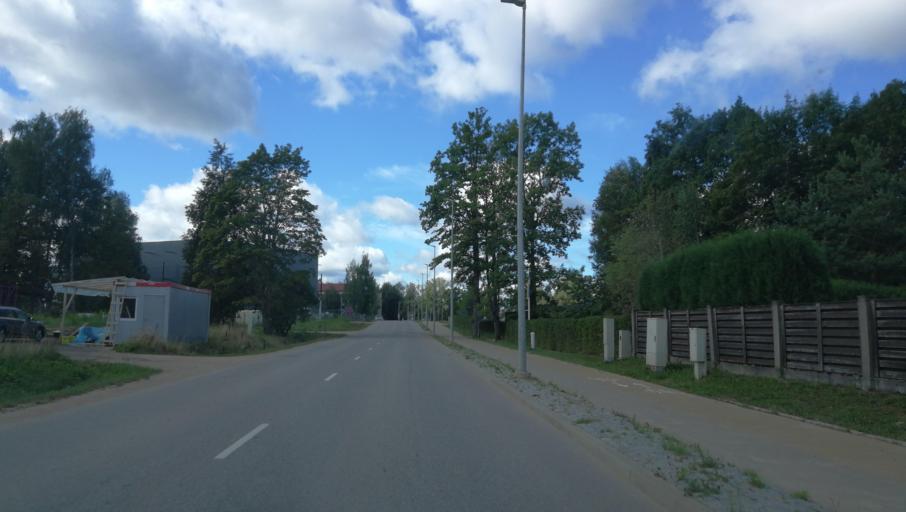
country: LV
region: Cesu Rajons
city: Cesis
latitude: 57.3027
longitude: 25.2388
